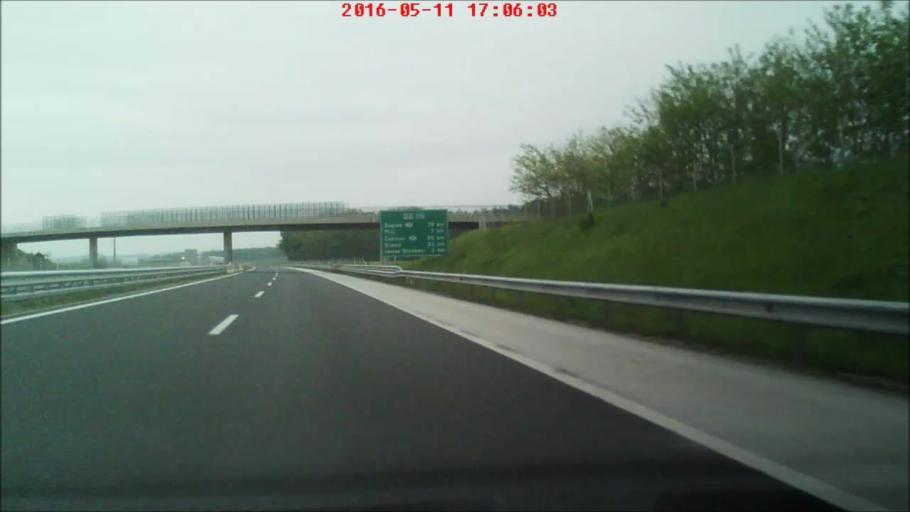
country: SI
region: Kidricevo
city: Kidricevo
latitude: 46.4079
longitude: 15.8169
